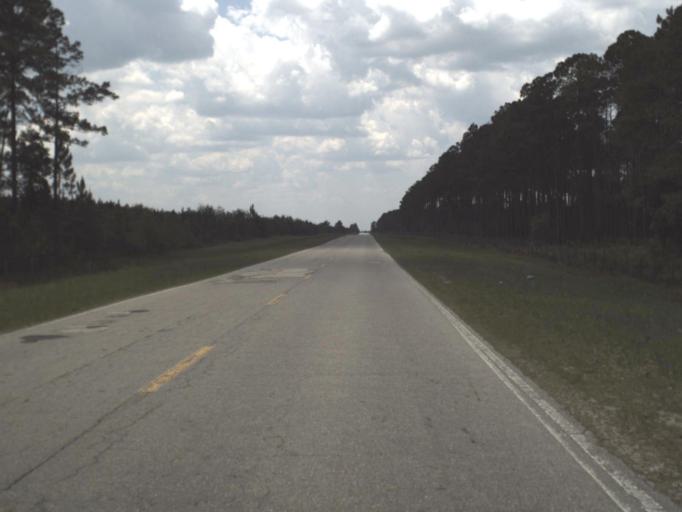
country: US
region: Florida
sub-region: Bradford County
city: Starke
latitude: 29.9880
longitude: -82.0203
